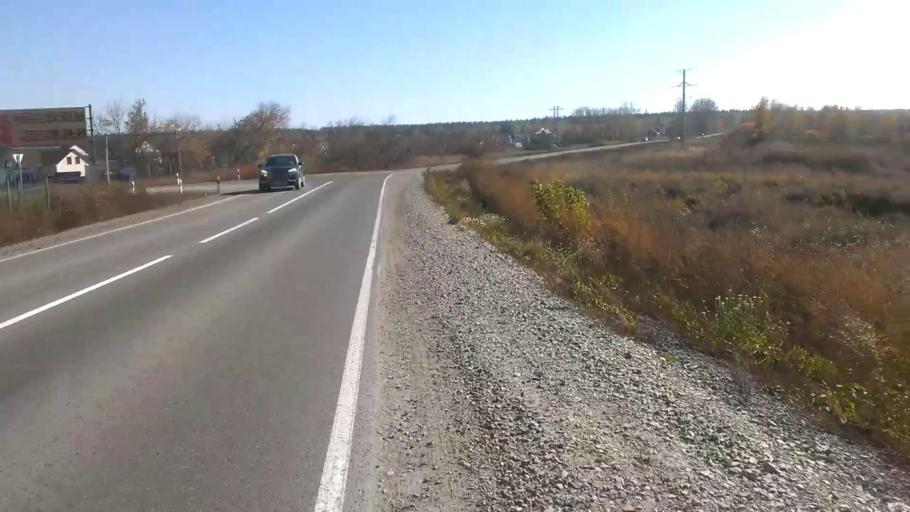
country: RU
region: Altai Krai
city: Sannikovo
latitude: 53.3123
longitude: 83.9645
